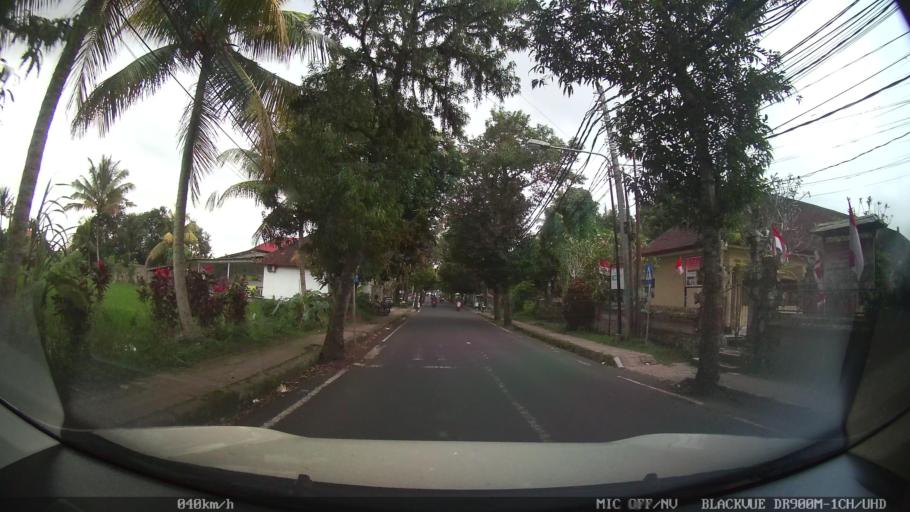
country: ID
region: Bali
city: Bunutan
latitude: -8.4870
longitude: 115.2538
